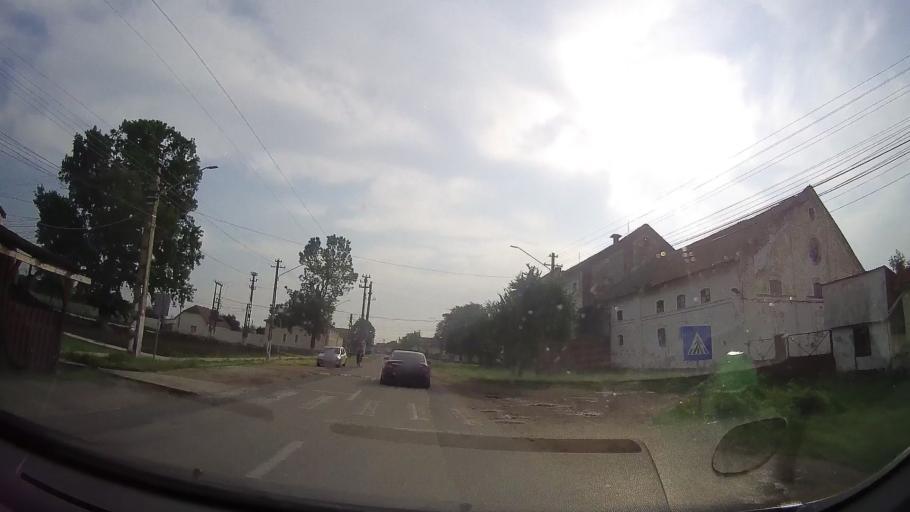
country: RO
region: Timis
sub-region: Comuna Peciu Nou
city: Peciu Nou
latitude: 45.6003
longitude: 21.0527
